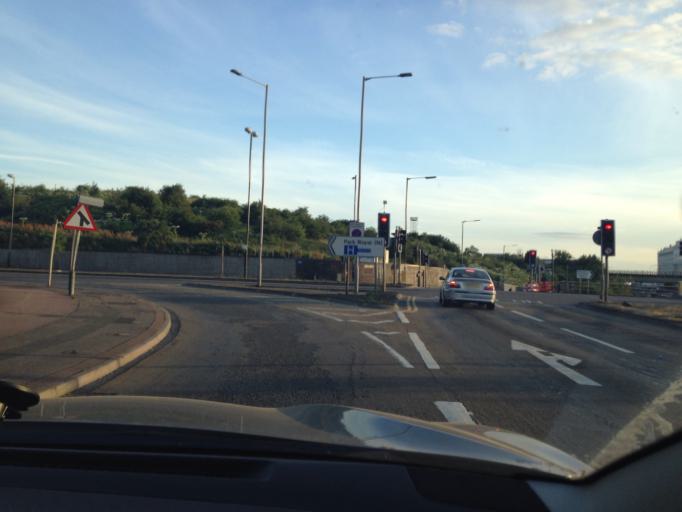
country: GB
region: England
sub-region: Greater London
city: Wembley
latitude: 51.5395
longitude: -0.2776
